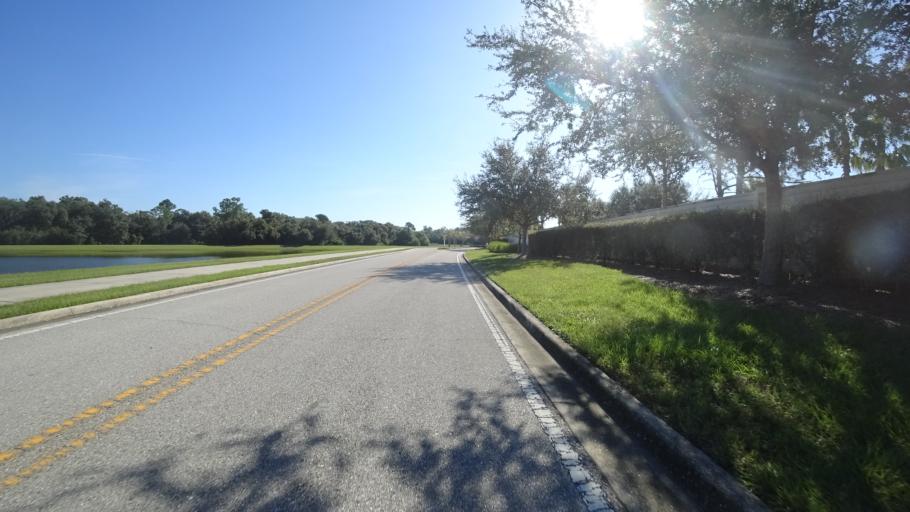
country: US
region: Florida
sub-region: Sarasota County
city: The Meadows
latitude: 27.4177
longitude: -82.4025
